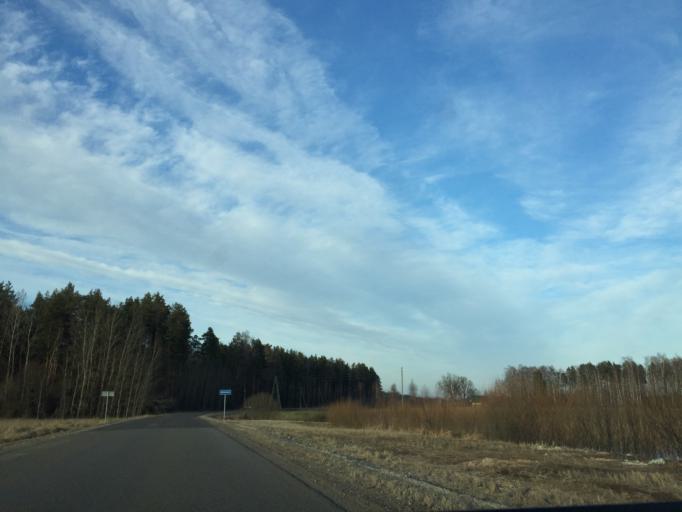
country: LV
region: Kekava
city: Kekava
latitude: 56.8176
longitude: 24.1844
